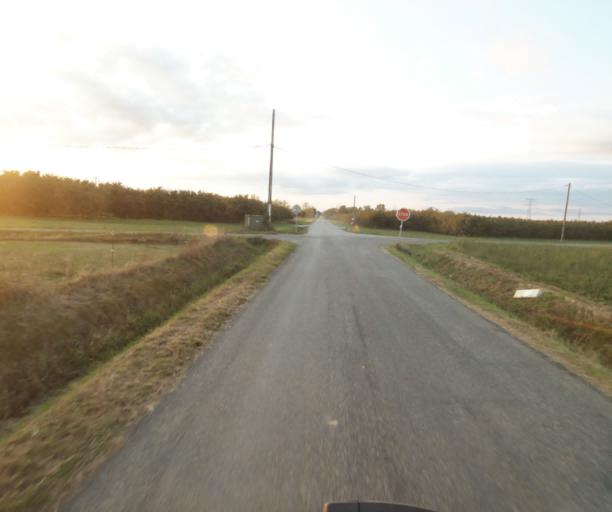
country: FR
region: Midi-Pyrenees
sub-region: Departement du Tarn-et-Garonne
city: Verdun-sur-Garonne
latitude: 43.8308
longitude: 1.2269
